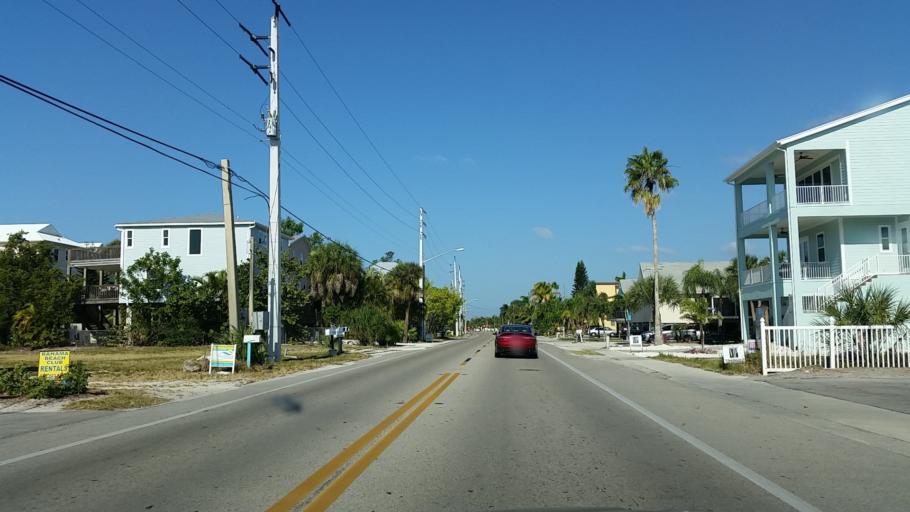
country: US
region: Florida
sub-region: Lee County
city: Fort Myers Beach
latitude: 26.4320
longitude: -81.9151
